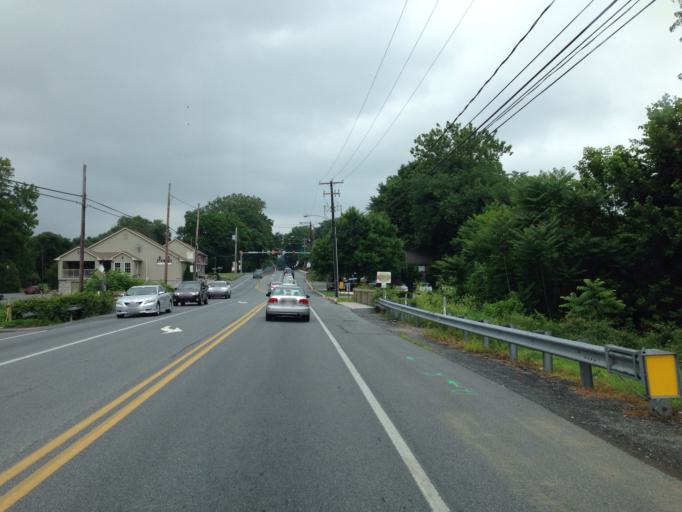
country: US
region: Pennsylvania
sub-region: Lancaster County
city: Lancaster
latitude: 40.0380
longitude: -76.3435
